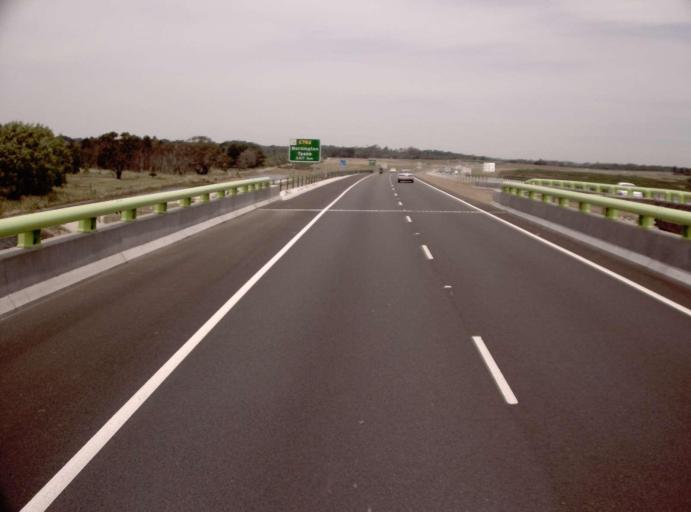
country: AU
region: Victoria
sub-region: Mornington Peninsula
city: Moorooduc
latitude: -38.2391
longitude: 145.1237
